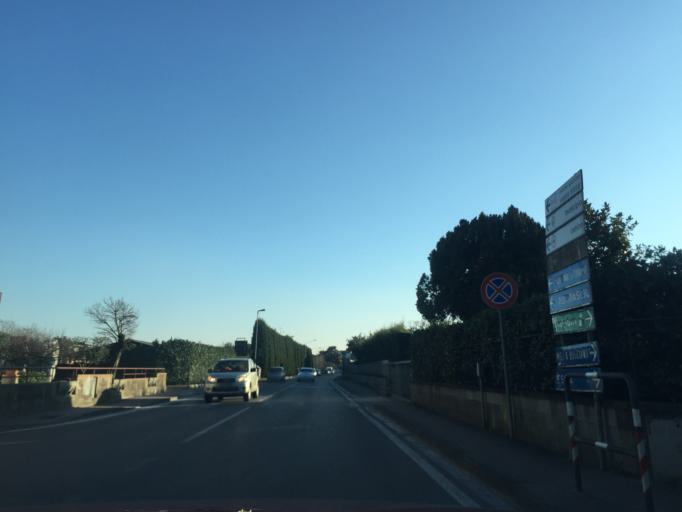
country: IT
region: Tuscany
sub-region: Provincia di Pistoia
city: Ponte Buggianese
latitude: 43.8468
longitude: 10.7468
